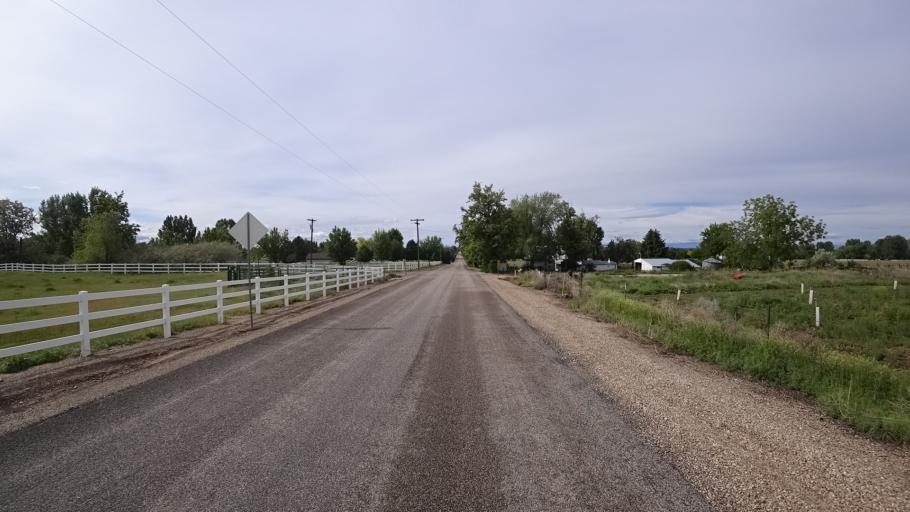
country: US
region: Idaho
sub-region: Ada County
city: Eagle
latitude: 43.7341
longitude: -116.4034
